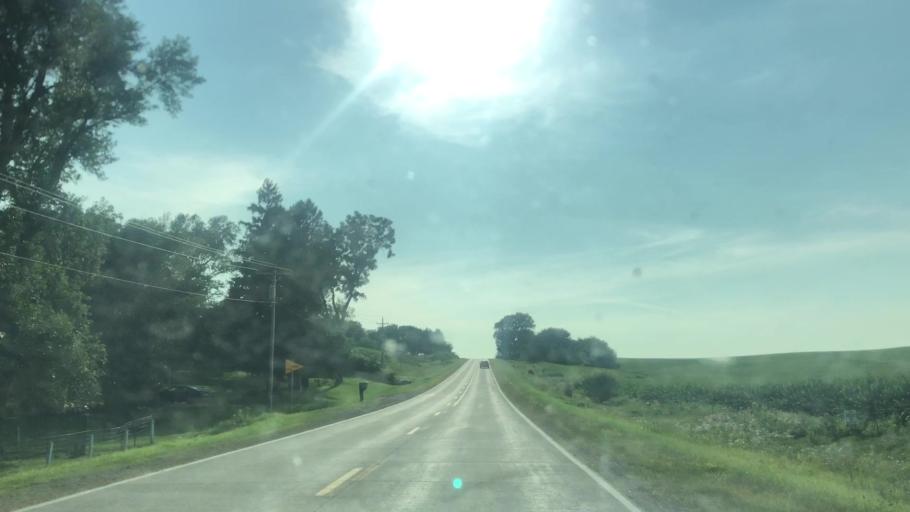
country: US
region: Iowa
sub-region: Marshall County
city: Marshalltown
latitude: 42.0489
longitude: -92.9712
